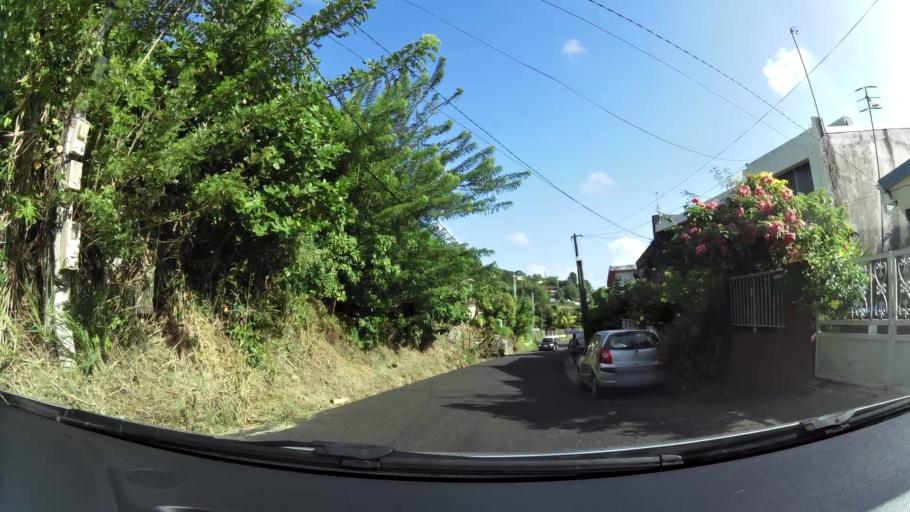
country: MQ
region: Martinique
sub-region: Martinique
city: La Trinite
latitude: 14.7379
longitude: -60.9667
